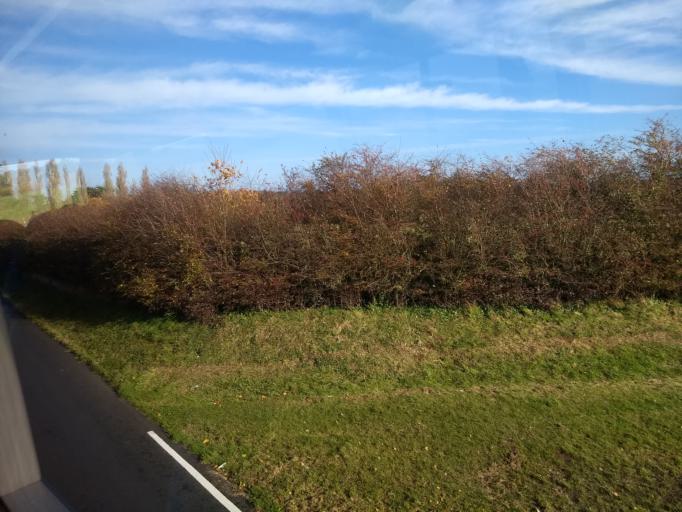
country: GB
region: England
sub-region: Isle of Wight
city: Yarmouth
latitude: 50.6983
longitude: -1.4820
